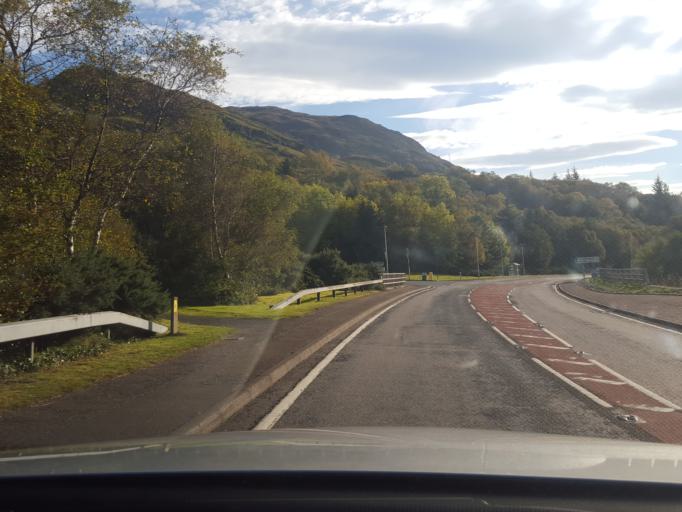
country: GB
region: Scotland
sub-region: Highland
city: Fort William
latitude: 57.2769
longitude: -5.5150
